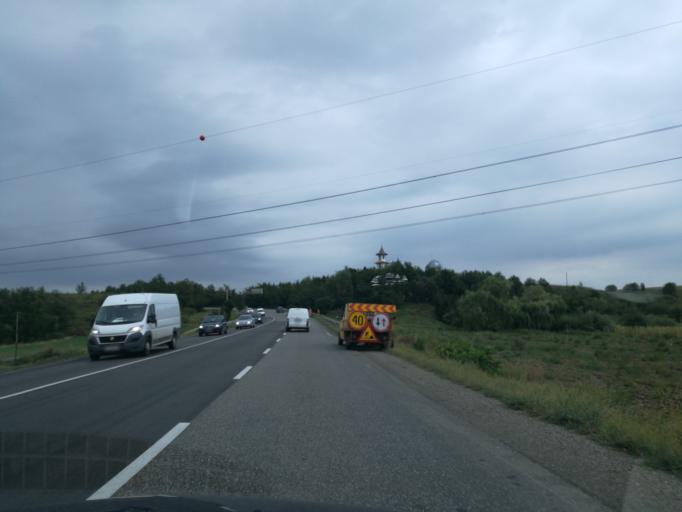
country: RO
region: Suceava
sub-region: Comuna Vadu Moldovei
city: Dumbravita
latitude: 47.4000
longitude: 26.3240
